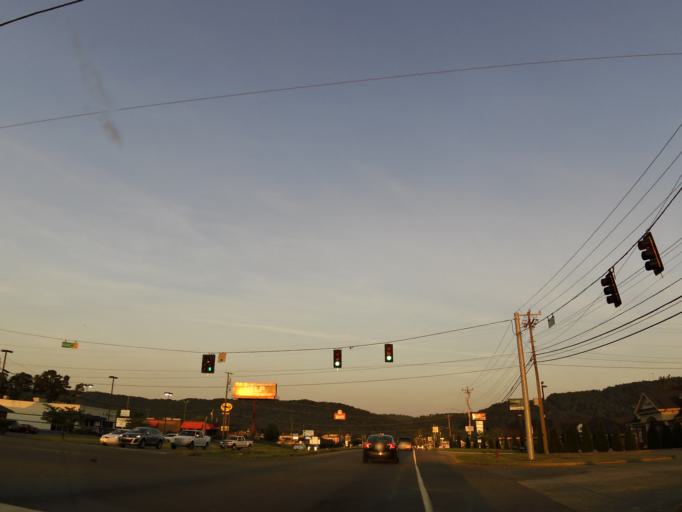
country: US
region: Tennessee
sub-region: Hamilton County
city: Collegedale
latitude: 35.0839
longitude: -85.0622
